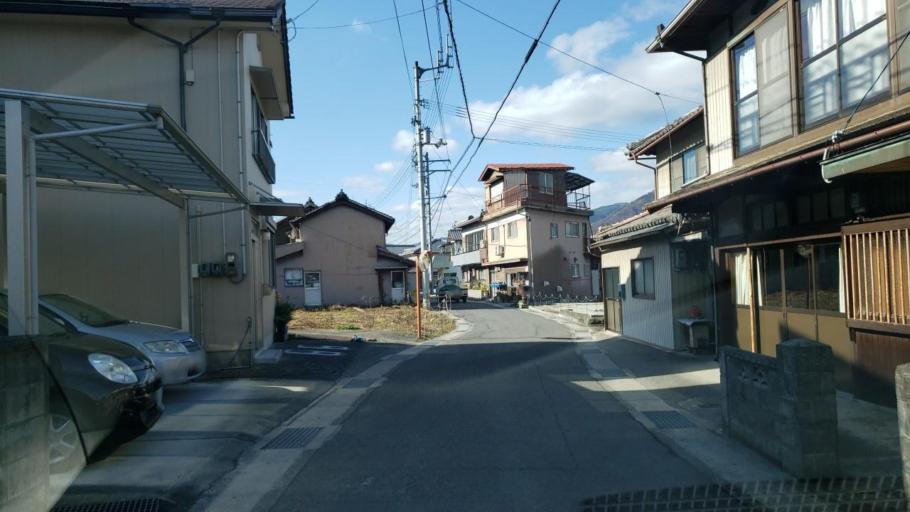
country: JP
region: Tokushima
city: Wakimachi
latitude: 34.0407
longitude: 134.0326
